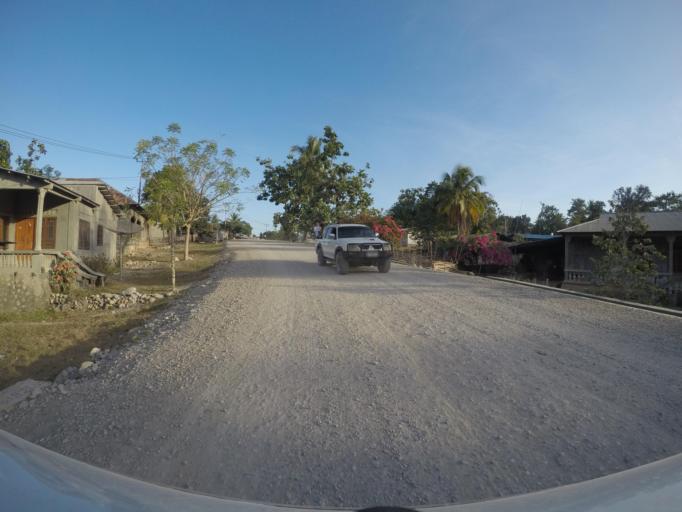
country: TL
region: Viqueque
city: Viqueque
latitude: -8.8399
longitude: 126.5163
